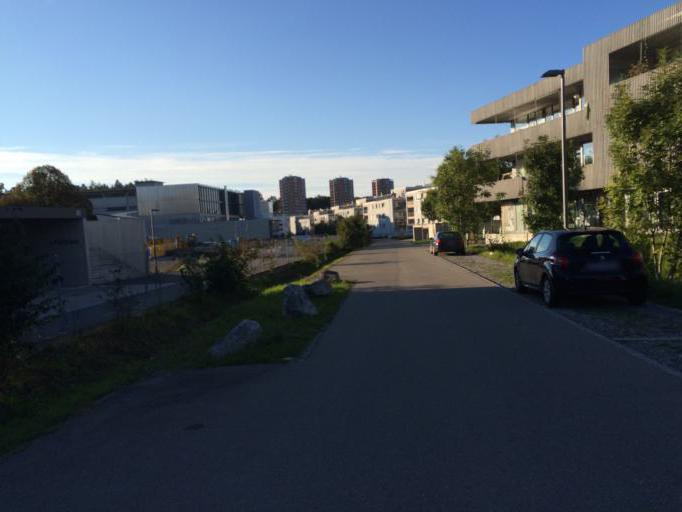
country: CH
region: Bern
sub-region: Bern-Mittelland District
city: Koniz
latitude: 46.9340
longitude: 7.4201
